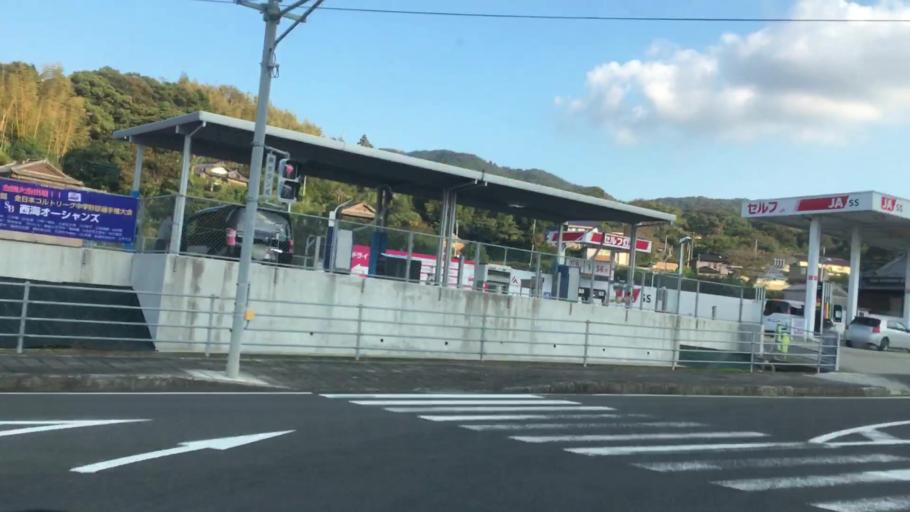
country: JP
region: Nagasaki
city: Sasebo
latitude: 33.0391
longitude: 129.6592
